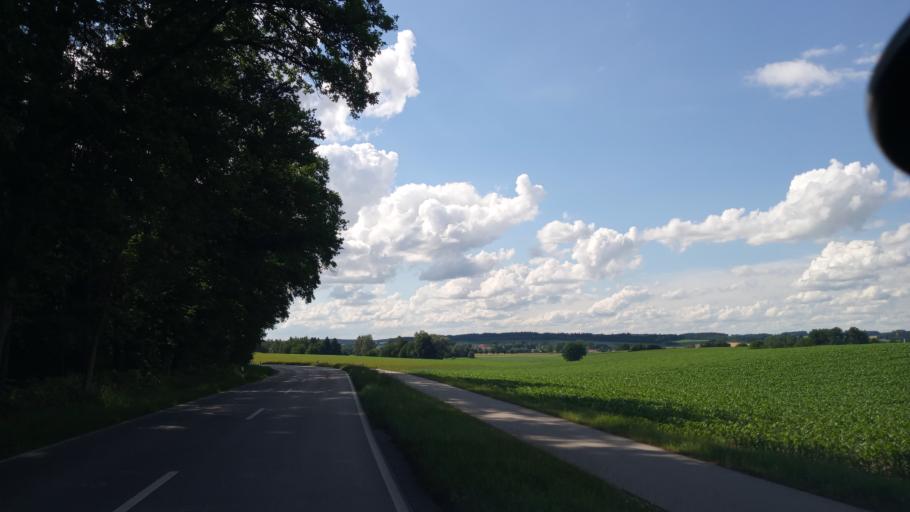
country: DE
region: Bavaria
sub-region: Upper Bavaria
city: Markt Indersdorf
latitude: 48.3552
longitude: 11.4067
